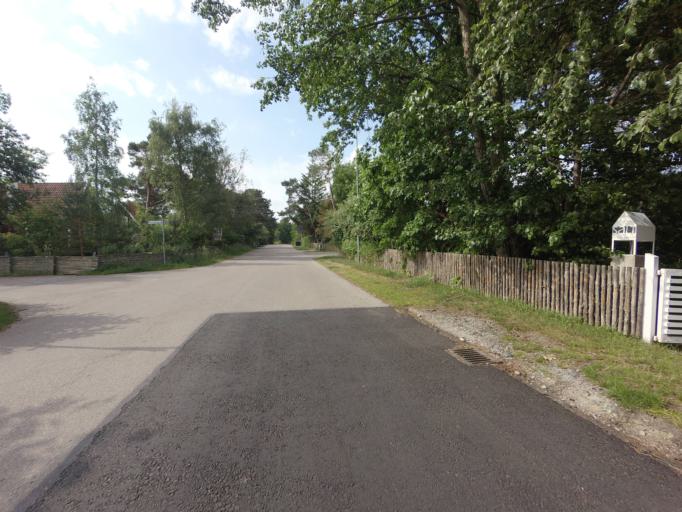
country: SE
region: Skane
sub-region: Angelholms Kommun
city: AEngelholm
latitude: 56.2594
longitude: 12.8360
